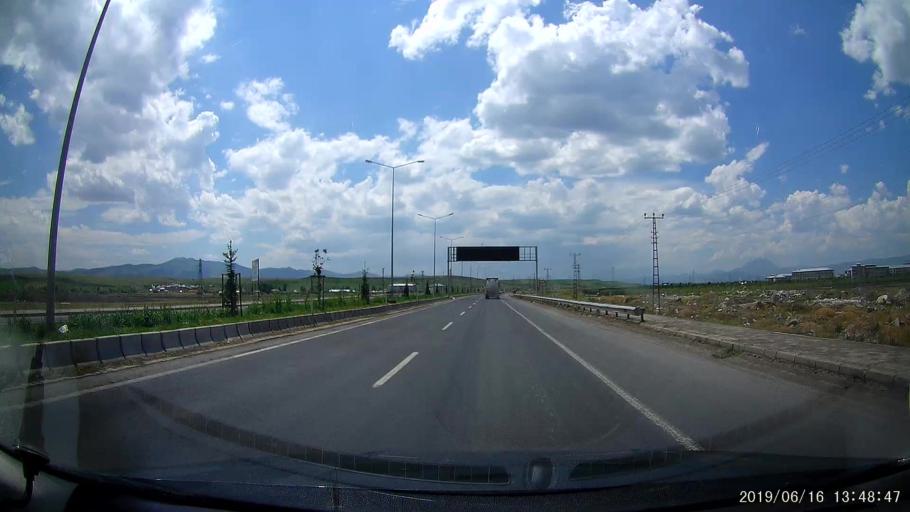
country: TR
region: Agri
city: Agri
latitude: 39.7147
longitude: 43.0013
